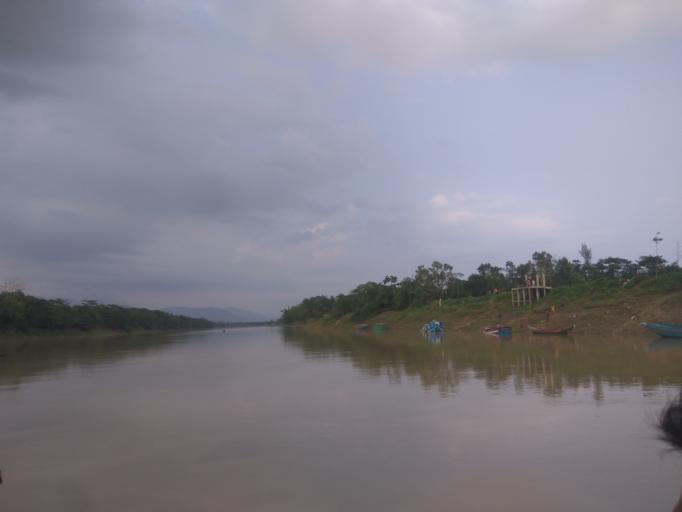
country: IN
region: Assam
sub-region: Karimganj
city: Karimganj
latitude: 24.9880
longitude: 92.4002
